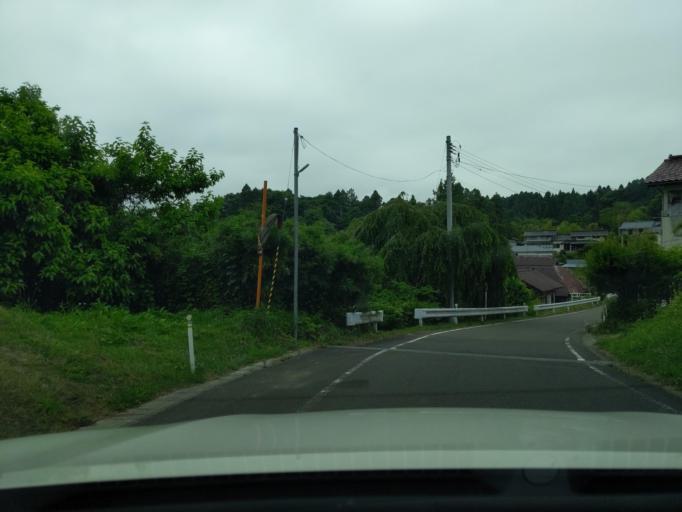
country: JP
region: Fukushima
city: Miharu
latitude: 37.4127
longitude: 140.4421
